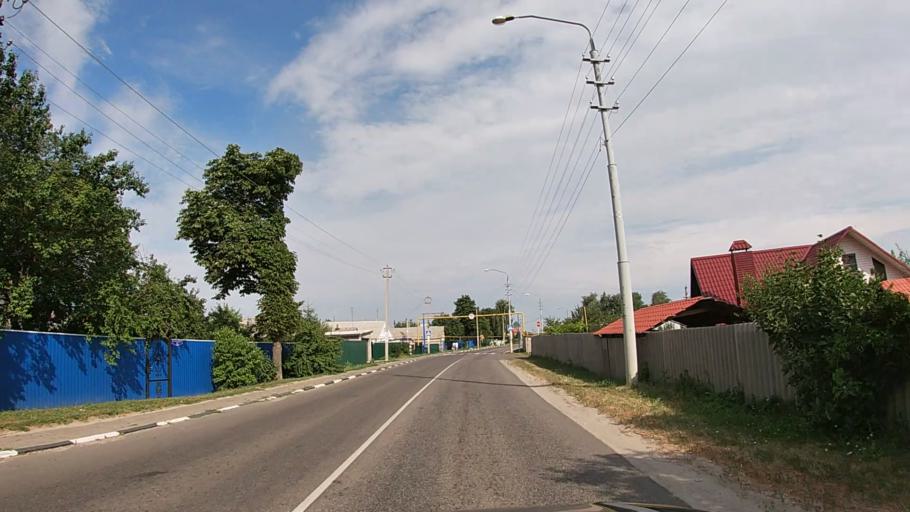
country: RU
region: Belgorod
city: Krasnaya Yaruga
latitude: 50.8003
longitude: 35.6616
